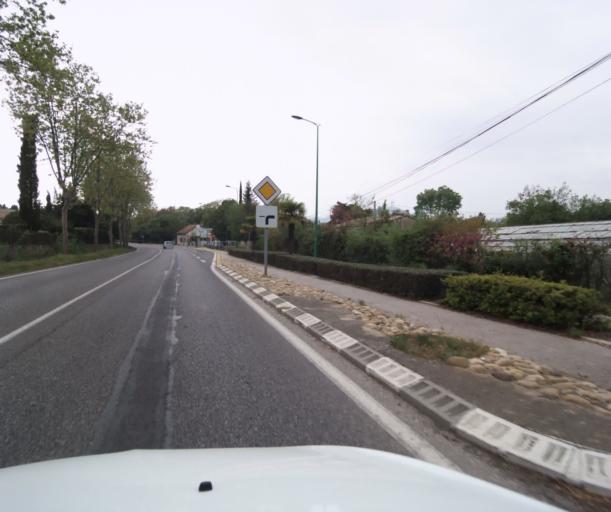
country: FR
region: Provence-Alpes-Cote d'Azur
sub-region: Departement du Var
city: La Garde
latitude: 43.1091
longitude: 6.0029
